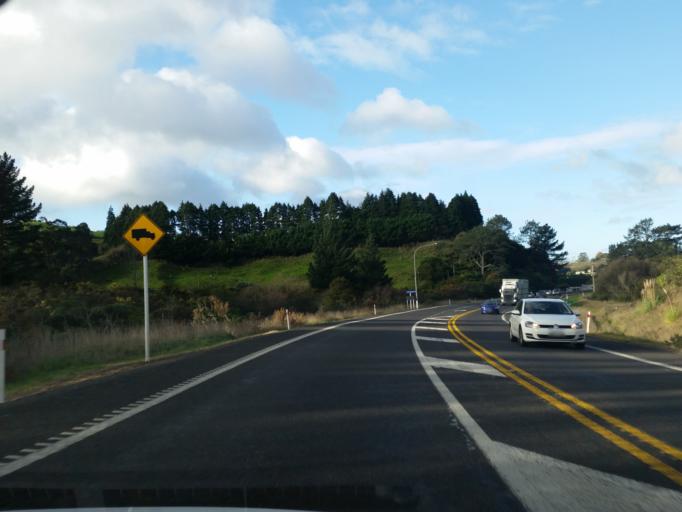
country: NZ
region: Bay of Plenty
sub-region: Western Bay of Plenty District
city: Katikati
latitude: -37.6489
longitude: 175.9746
